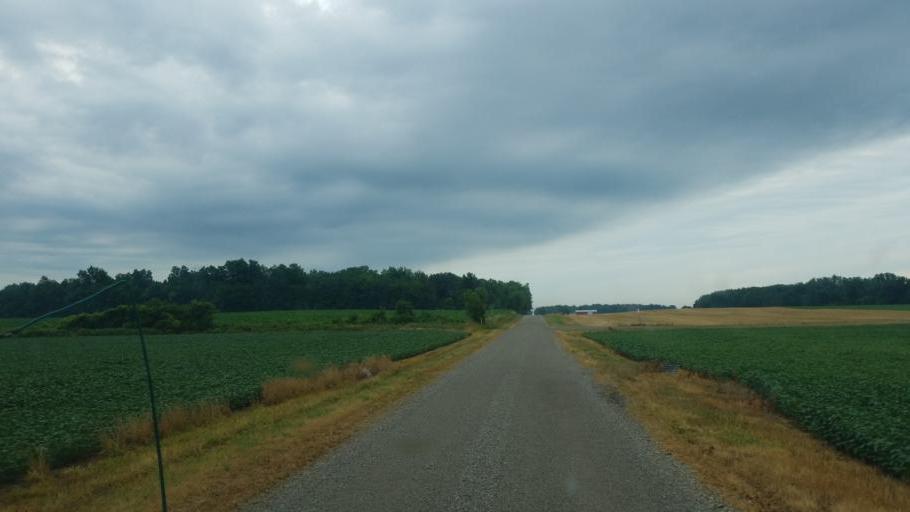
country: US
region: Indiana
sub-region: Steuben County
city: Hamilton
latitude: 41.4943
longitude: -84.9110
